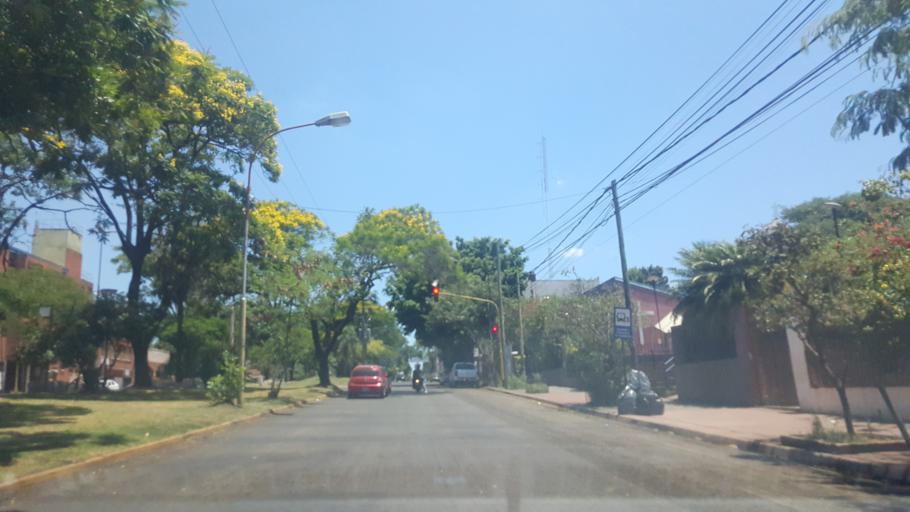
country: AR
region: Misiones
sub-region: Departamento de Capital
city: Posadas
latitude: -27.3712
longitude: -55.9020
